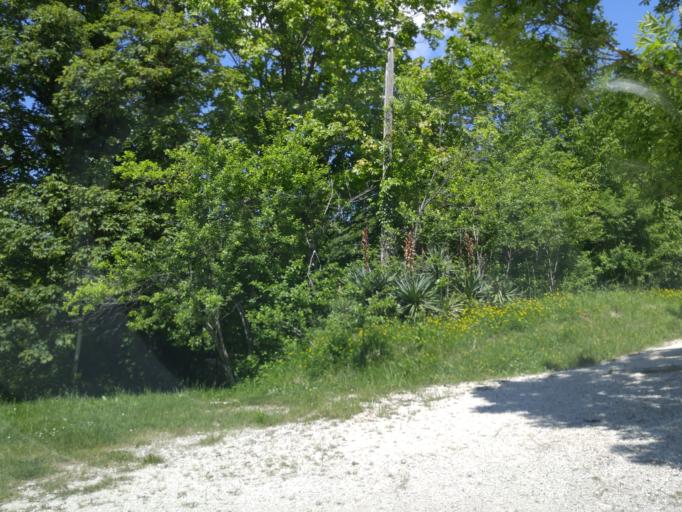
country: IT
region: The Marches
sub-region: Provincia di Pesaro e Urbino
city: Canavaccio
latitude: 43.7120
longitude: 12.6912
